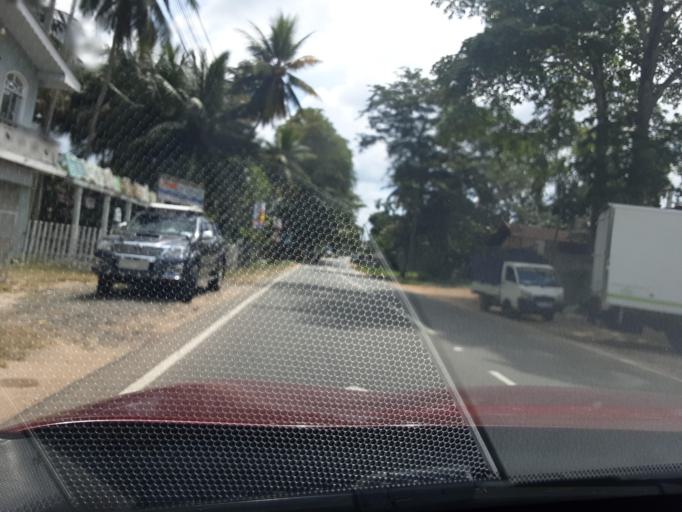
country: LK
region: North Western
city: Kuliyapitiya
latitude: 7.4506
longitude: 80.1869
